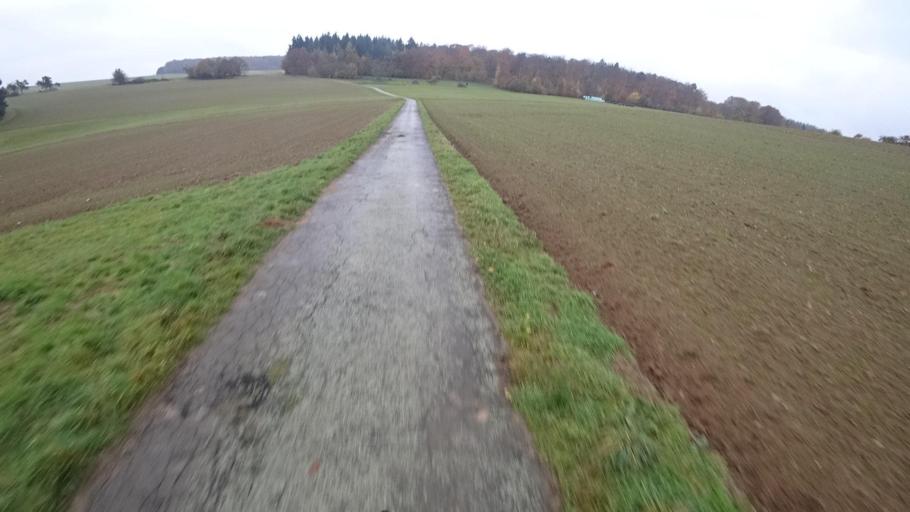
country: DE
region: Rheinland-Pfalz
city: Sankt Goar
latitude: 50.1400
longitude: 7.6945
